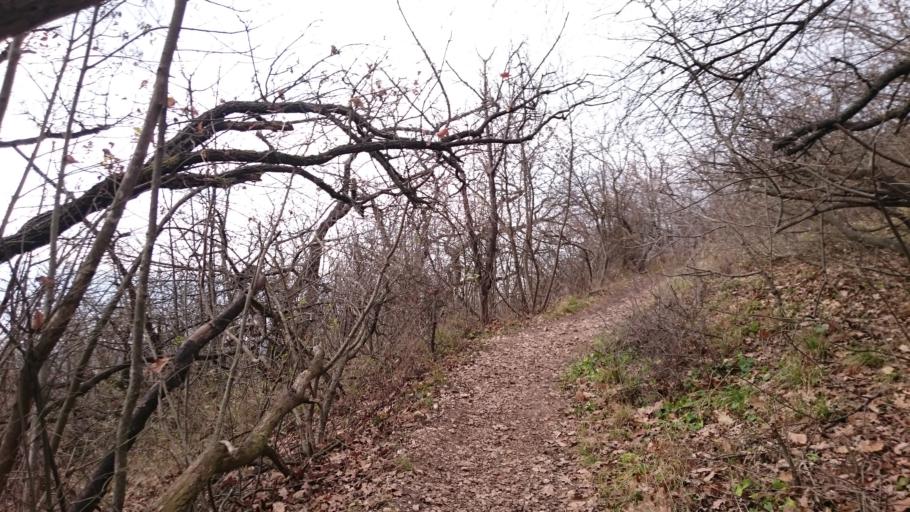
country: HU
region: Pest
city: Pilisborosjeno
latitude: 47.6207
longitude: 18.9878
